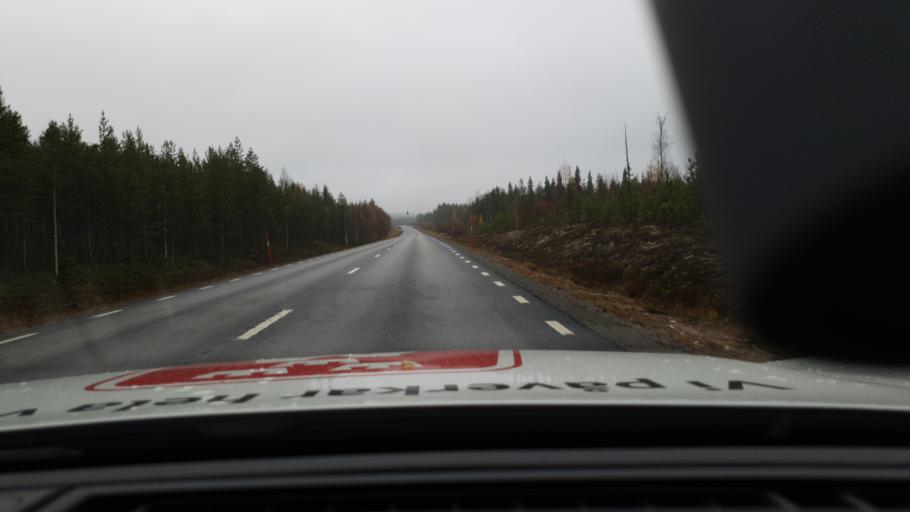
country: SE
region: Norrbotten
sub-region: Overkalix Kommun
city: OEverkalix
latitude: 66.6238
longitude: 22.2245
